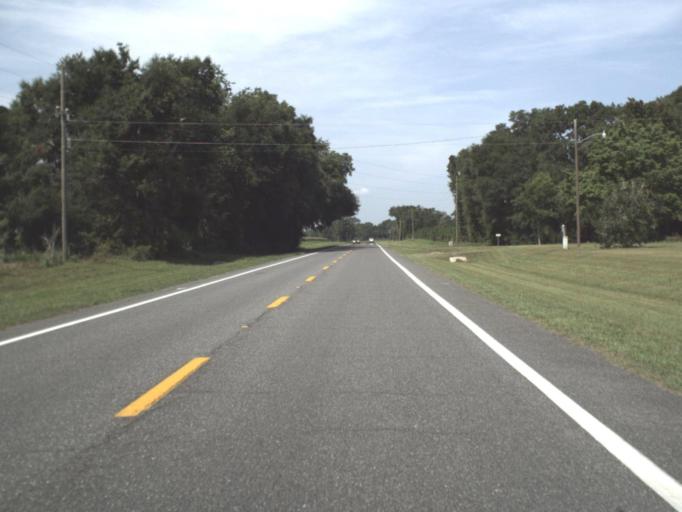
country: US
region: Florida
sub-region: Lafayette County
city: Mayo
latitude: 30.1832
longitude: -83.1335
